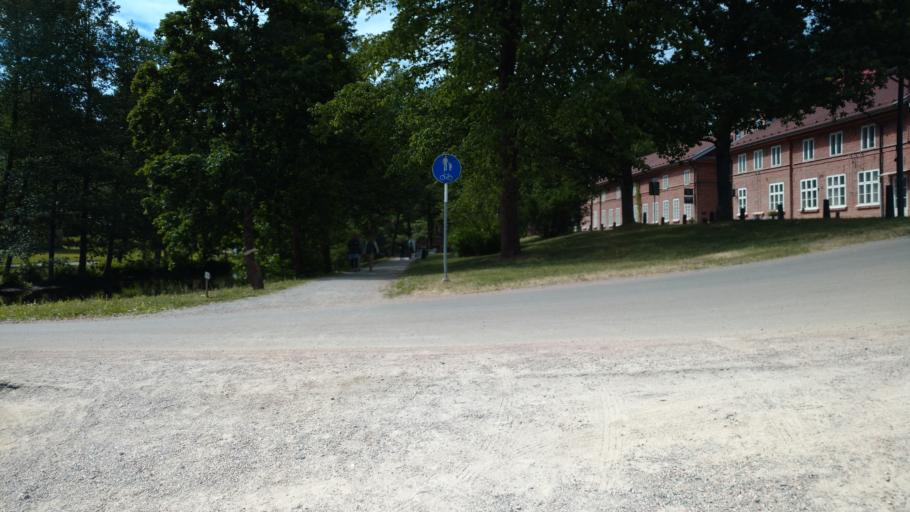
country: FI
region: Uusimaa
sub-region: Raaseporin
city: Pohja
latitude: 60.1296
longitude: 23.5426
